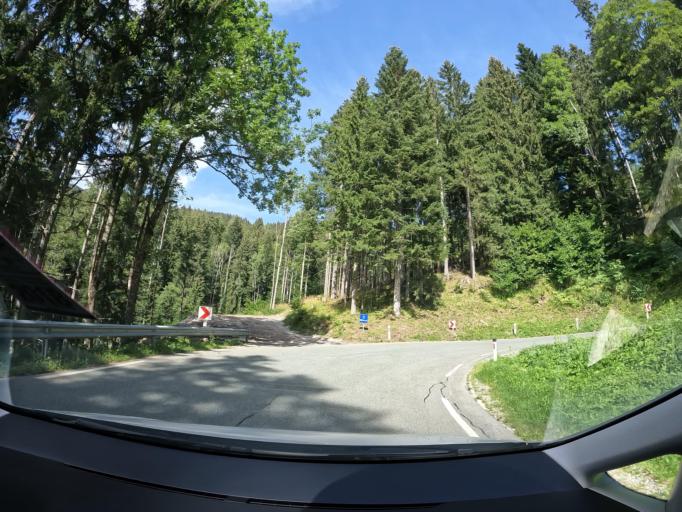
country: AT
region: Carinthia
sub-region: Politischer Bezirk Feldkirchen
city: Glanegg
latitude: 46.7509
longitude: 14.2163
